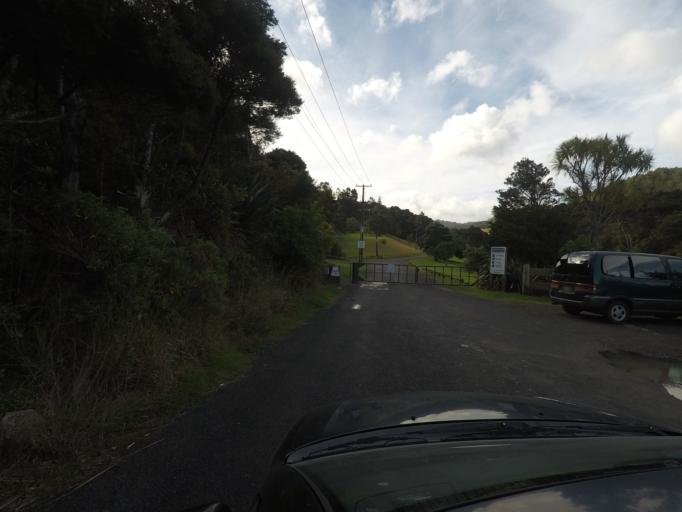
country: NZ
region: Auckland
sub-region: Auckland
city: Titirangi
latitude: -36.9954
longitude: 174.5668
